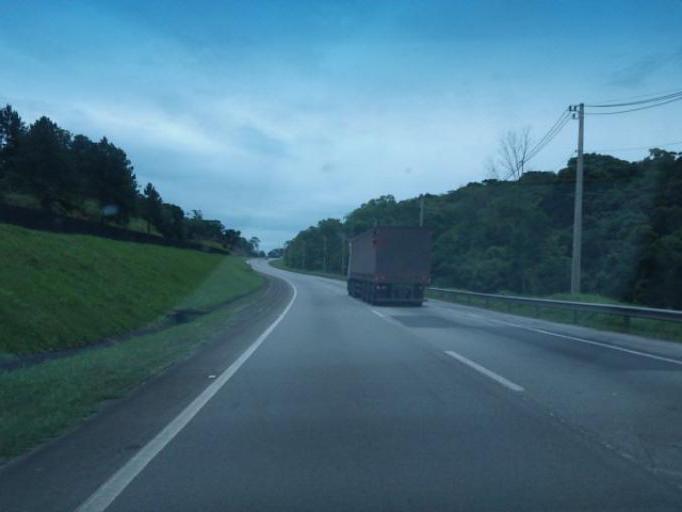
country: BR
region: Sao Paulo
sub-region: Juquitiba
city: Juquitiba
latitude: -23.9576
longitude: -47.1142
